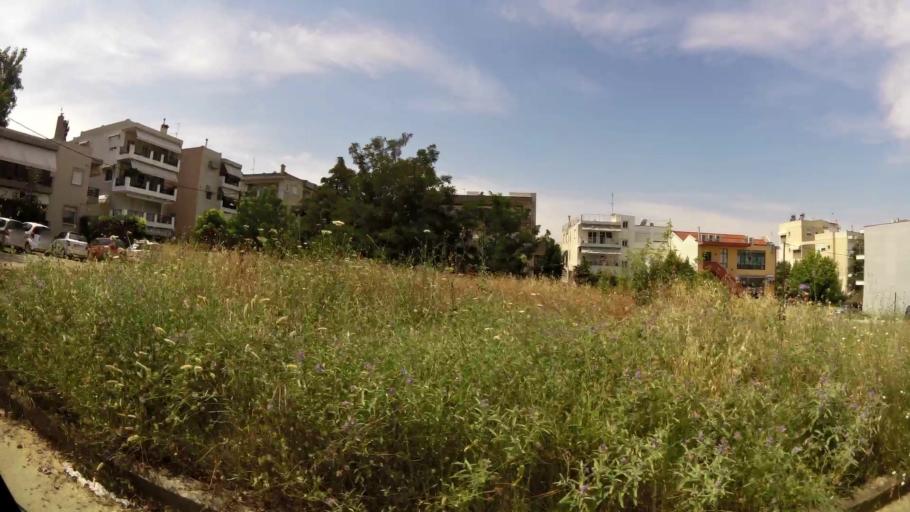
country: GR
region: Central Macedonia
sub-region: Nomos Thessalonikis
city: Pylaia
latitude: 40.6084
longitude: 22.9944
